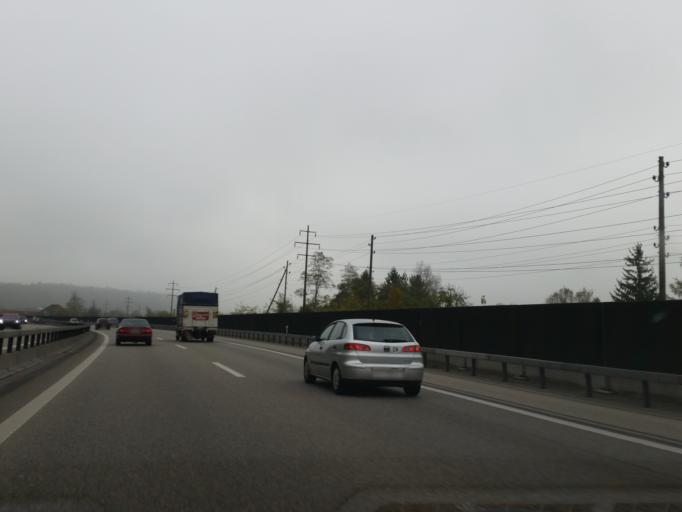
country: CH
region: Bern
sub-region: Oberaargau
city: Wangen an der Aare
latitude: 47.2380
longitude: 7.6419
